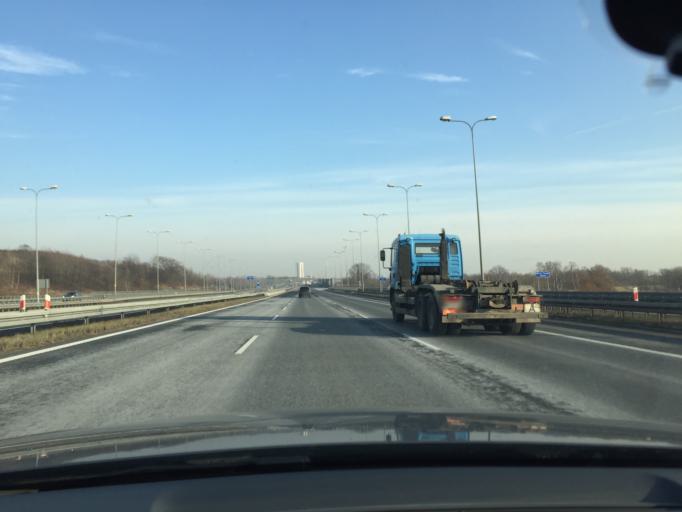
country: PL
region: Silesian Voivodeship
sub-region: Powiat gliwicki
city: Przyszowice
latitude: 50.2663
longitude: 18.7428
